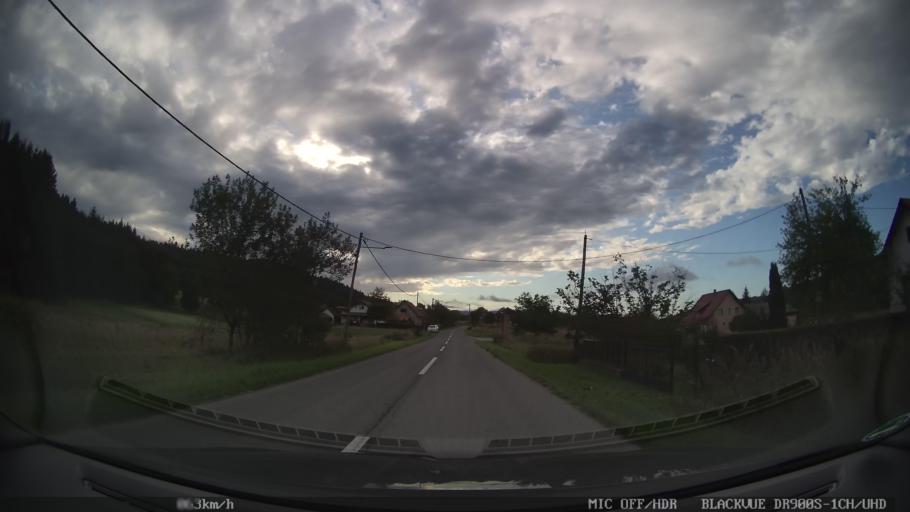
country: HR
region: Licko-Senjska
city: Jezerce
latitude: 44.9710
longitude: 15.5056
